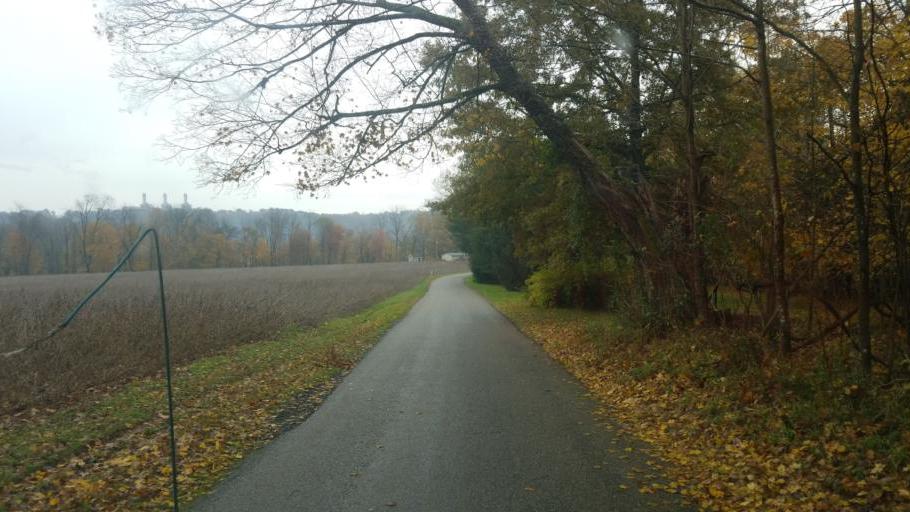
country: US
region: Ohio
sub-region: Washington County
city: Beverly
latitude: 39.5314
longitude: -81.7361
